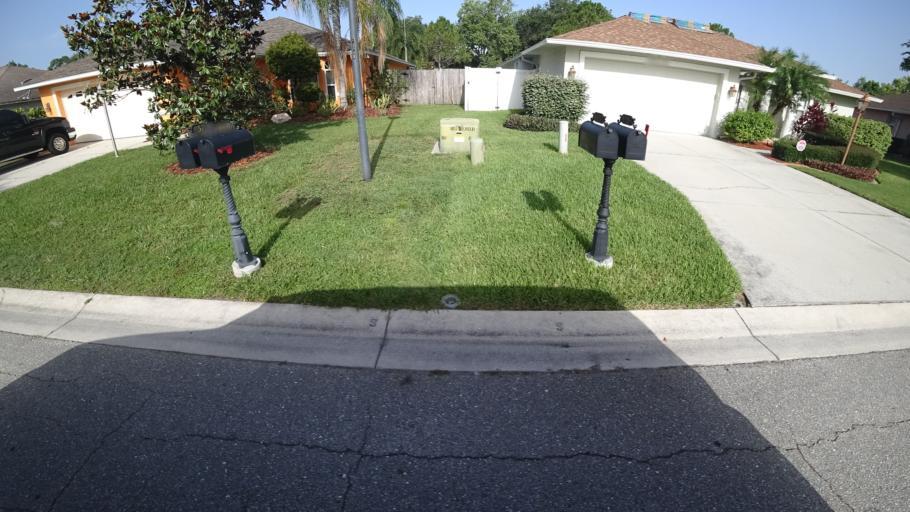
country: US
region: Florida
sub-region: Sarasota County
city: Desoto Lakes
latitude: 27.4238
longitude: -82.4747
